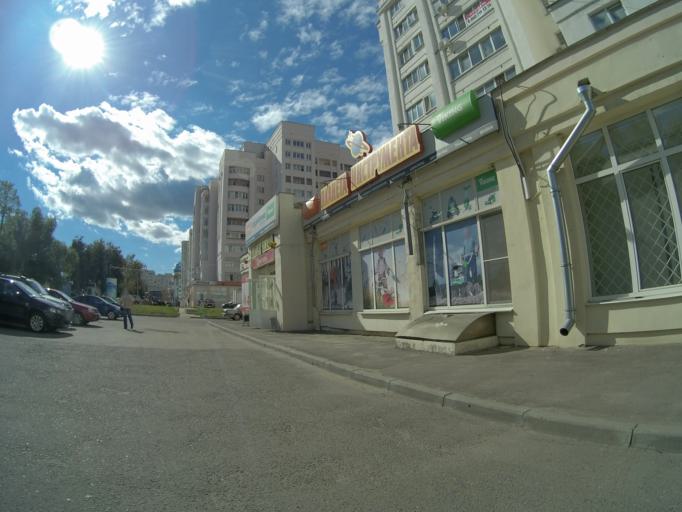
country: RU
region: Vladimir
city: Vladimir
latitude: 56.1191
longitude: 40.3570
